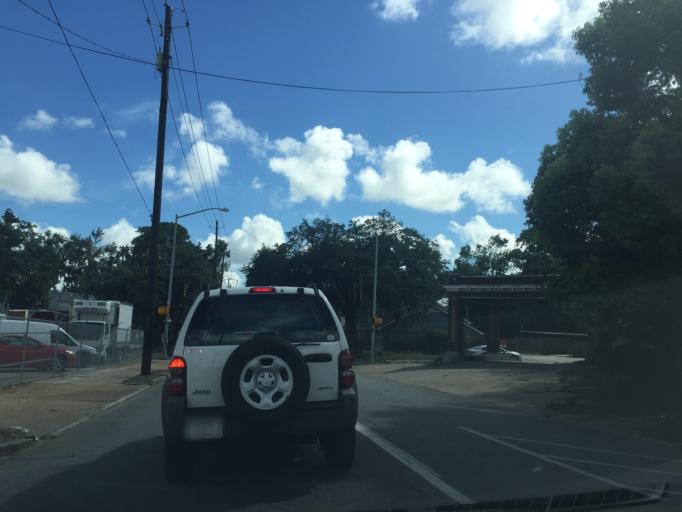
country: US
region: Georgia
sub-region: Chatham County
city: Savannah
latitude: 32.0562
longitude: -81.0946
